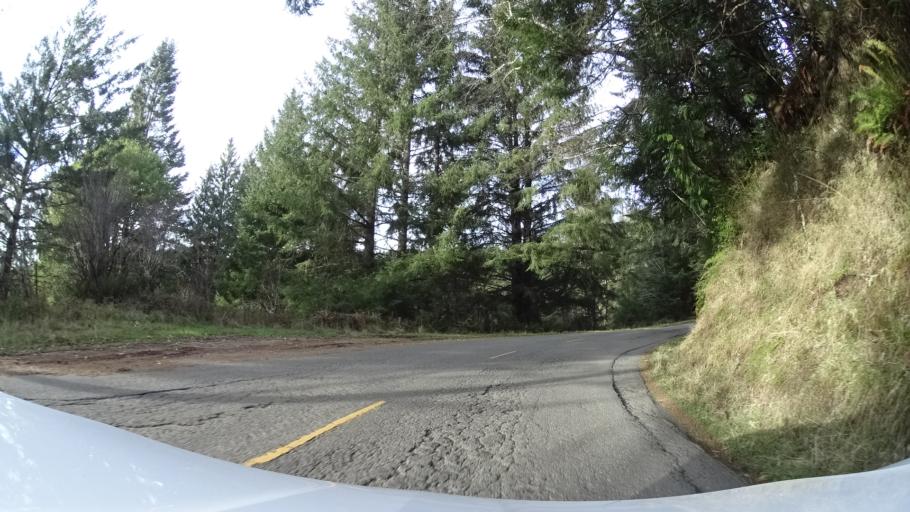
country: US
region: California
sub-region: Humboldt County
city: Ferndale
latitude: 40.5276
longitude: -124.2697
